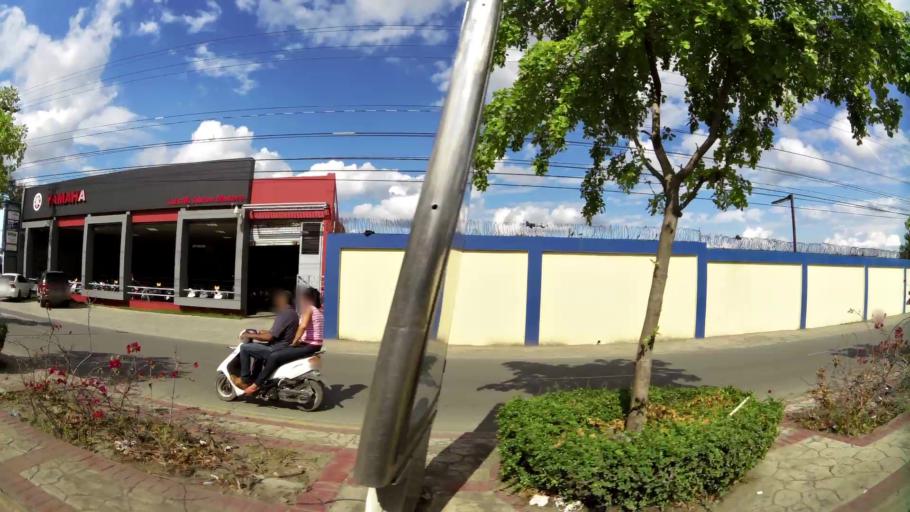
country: DO
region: La Vega
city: Concepcion de La Vega
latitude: 19.2303
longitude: -70.5281
